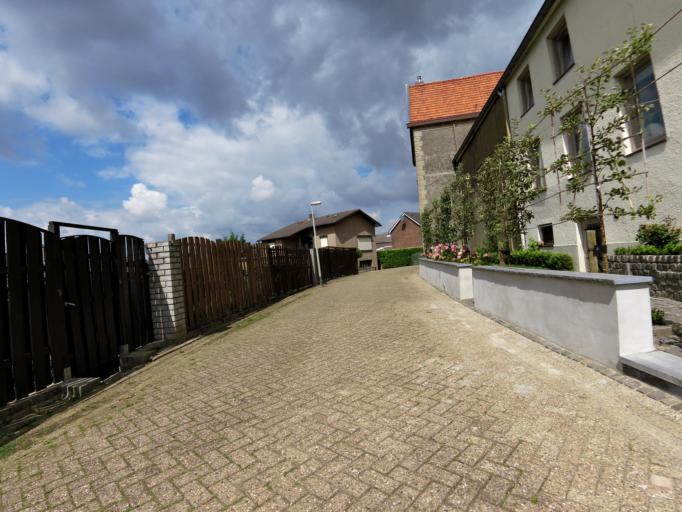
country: NL
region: Limburg
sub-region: Gemeente Simpelveld
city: Simpelveld
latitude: 50.8195
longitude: 6.0117
